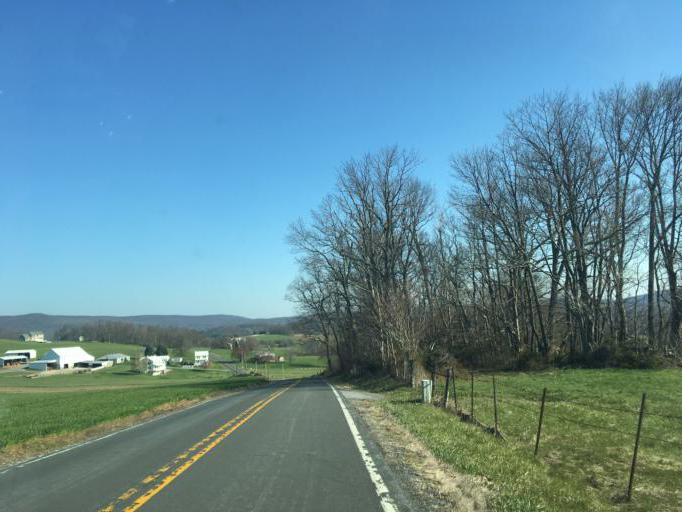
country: US
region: Maryland
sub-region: Frederick County
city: Myersville
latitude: 39.5550
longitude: -77.5490
